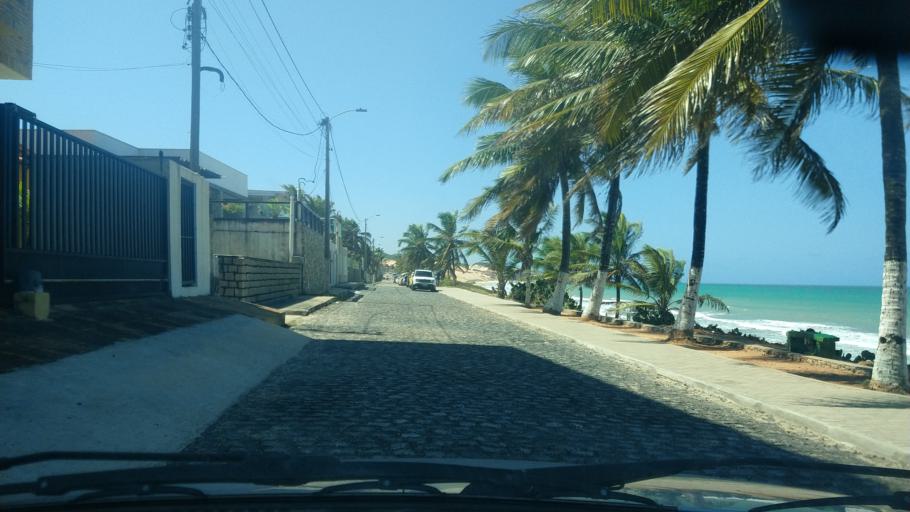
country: BR
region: Rio Grande do Norte
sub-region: Parnamirim
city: Parnamirim
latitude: -5.9539
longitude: -35.1518
